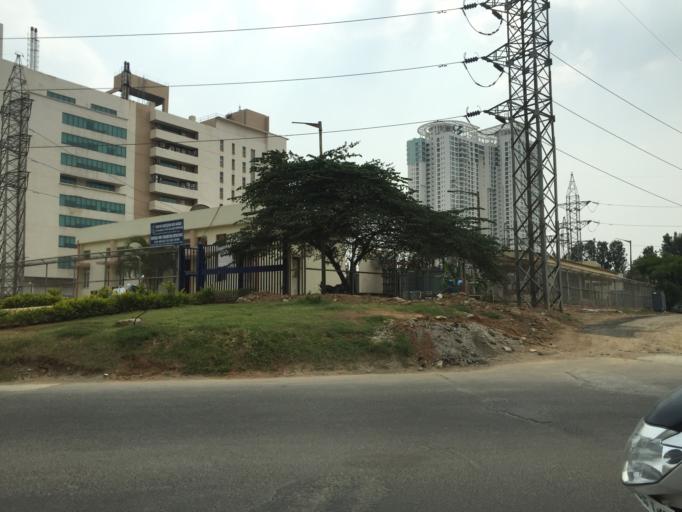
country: IN
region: Karnataka
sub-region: Bangalore Urban
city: Yelahanka
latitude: 13.0484
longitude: 77.6197
